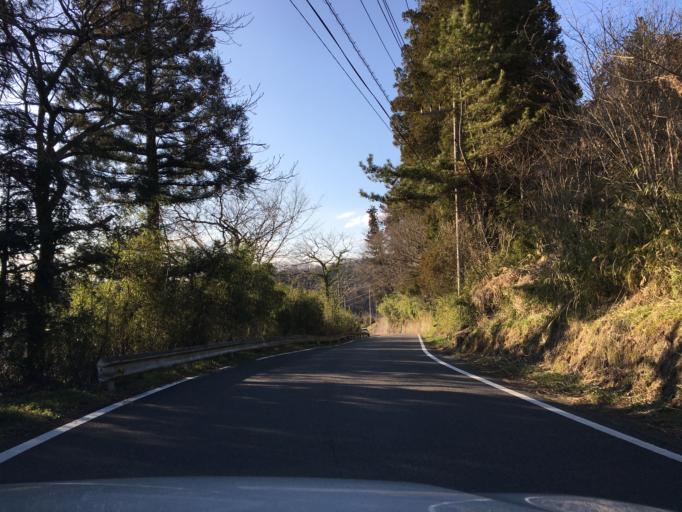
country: JP
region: Ibaraki
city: Daigo
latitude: 36.7738
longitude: 140.2496
